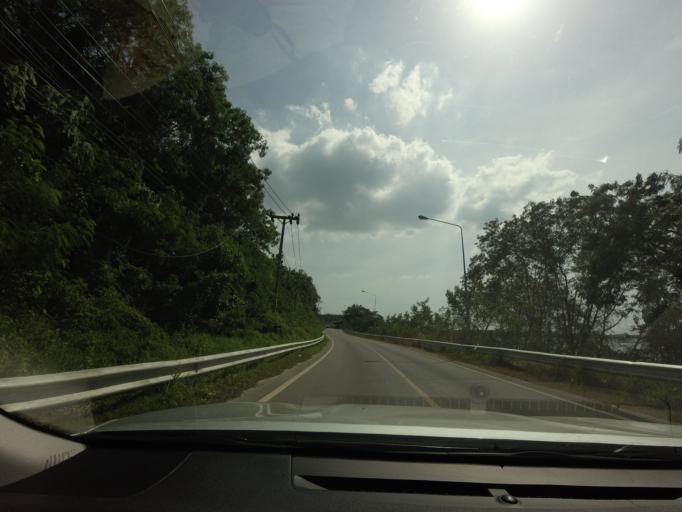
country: TH
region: Phangnga
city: Ban Ao Nang
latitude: 8.0698
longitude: 98.7445
